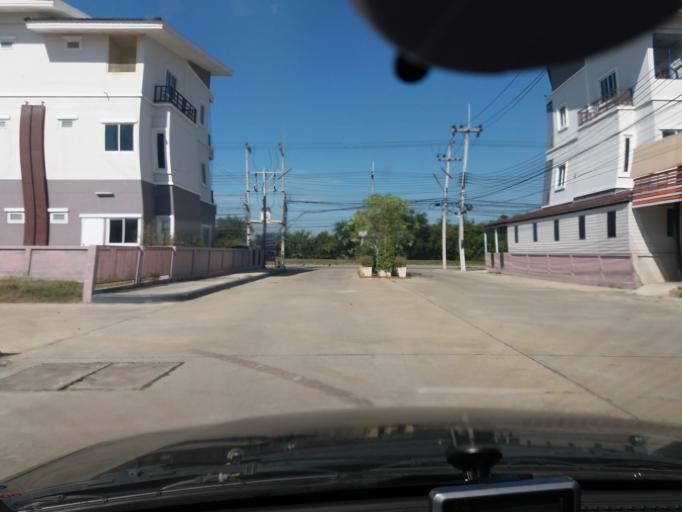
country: TH
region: Suphan Buri
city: Suphan Buri
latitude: 14.4617
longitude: 100.1464
